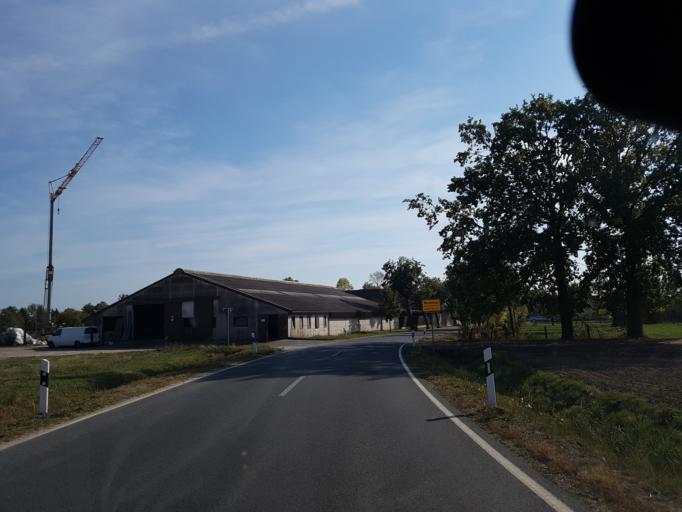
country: DE
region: Brandenburg
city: Doberlug-Kirchhain
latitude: 51.6564
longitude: 13.5287
